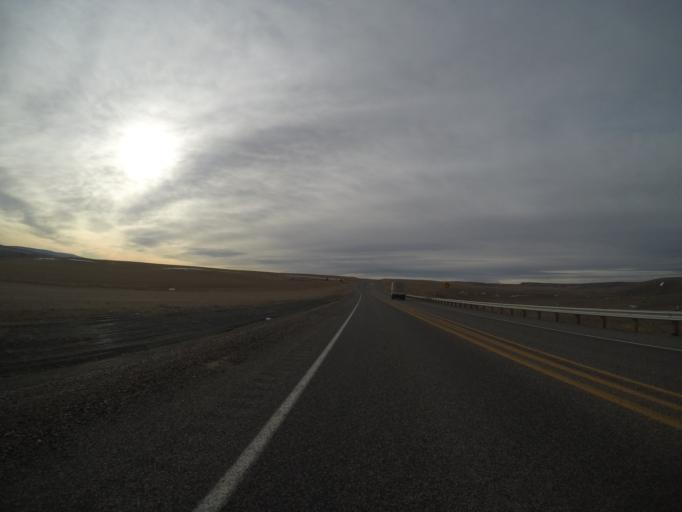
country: US
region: Montana
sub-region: Yellowstone County
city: Laurel
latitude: 45.5631
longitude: -108.8549
